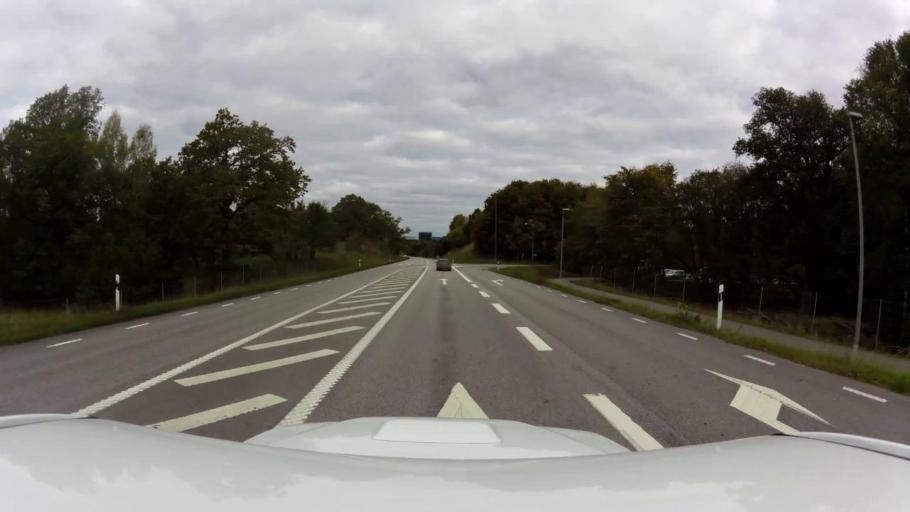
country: SE
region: OEstergoetland
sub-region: Kinda Kommun
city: Rimforsa
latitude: 58.2119
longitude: 15.6681
